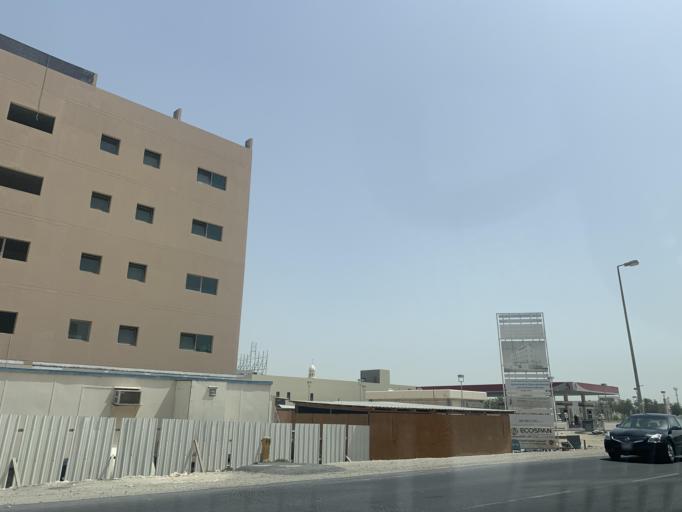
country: BH
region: Northern
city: Madinat `Isa
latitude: 26.1520
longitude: 50.5269
